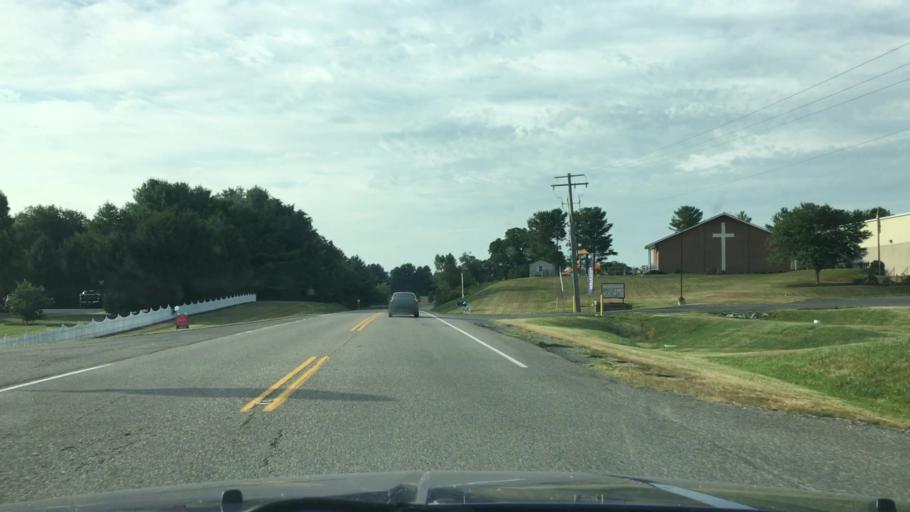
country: US
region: Virginia
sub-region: City of Waynesboro
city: Waynesboro
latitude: 38.1108
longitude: -78.9045
